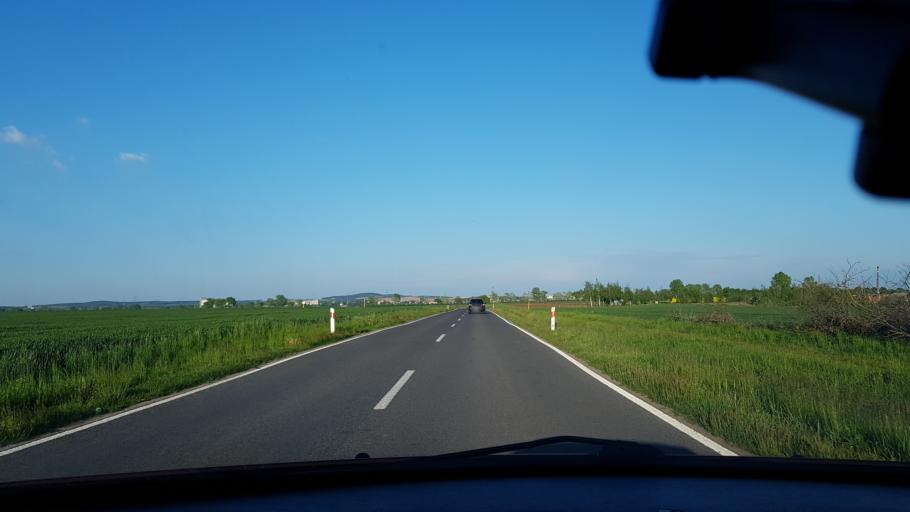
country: PL
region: Lower Silesian Voivodeship
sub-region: Powiat zabkowicki
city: Stoszowice
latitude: 50.5978
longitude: 16.7706
